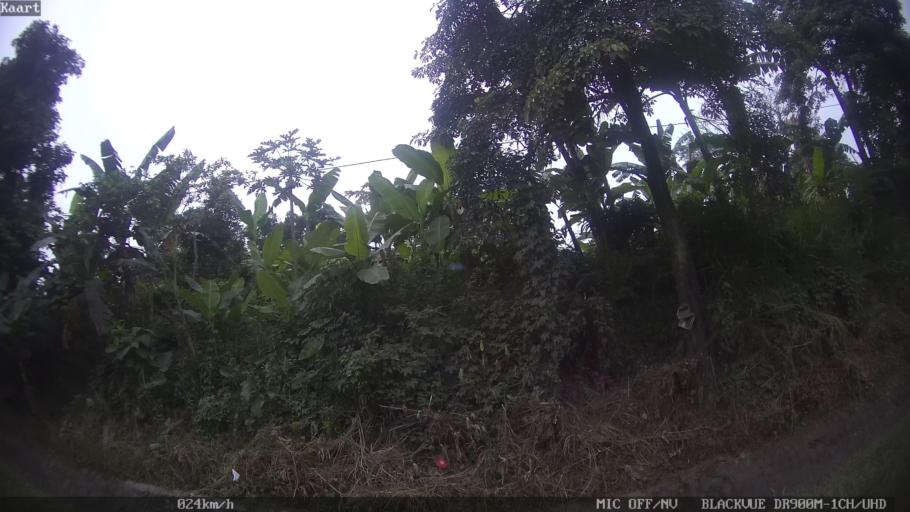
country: ID
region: Lampung
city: Panjang
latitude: -5.4386
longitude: 105.3198
